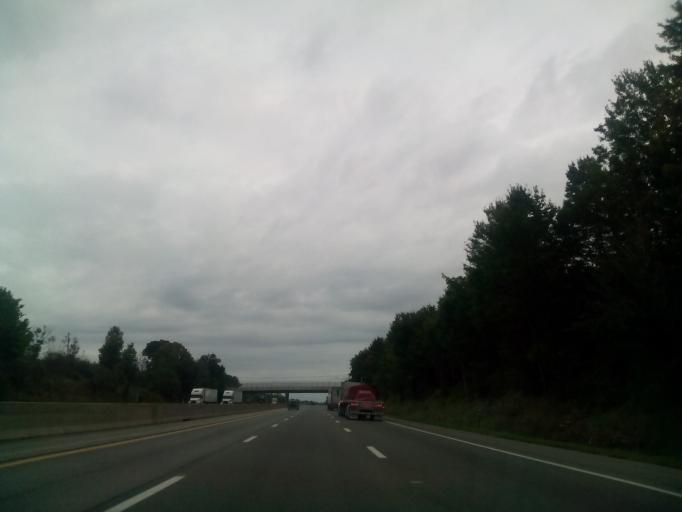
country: US
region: Ohio
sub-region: Huron County
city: Wakeman
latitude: 41.3334
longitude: -82.4112
